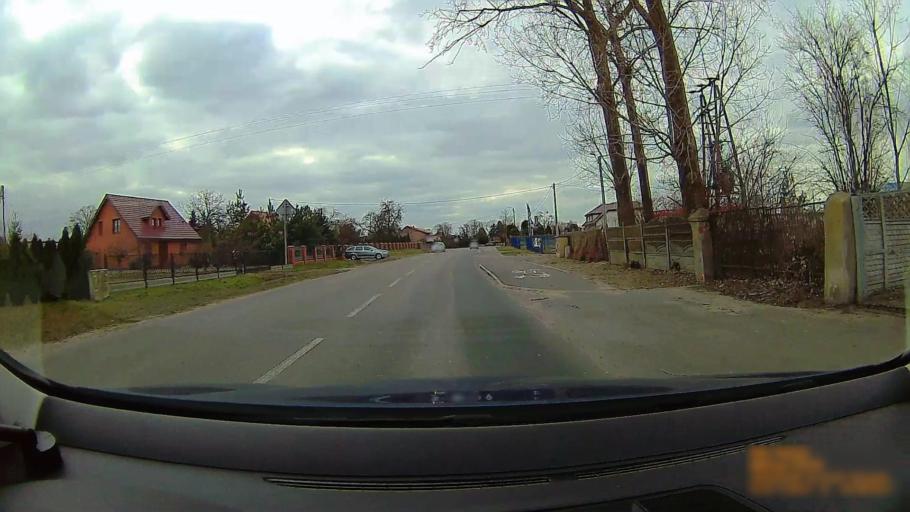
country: PL
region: Greater Poland Voivodeship
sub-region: Powiat koninski
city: Golina
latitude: 52.1971
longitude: 18.1383
